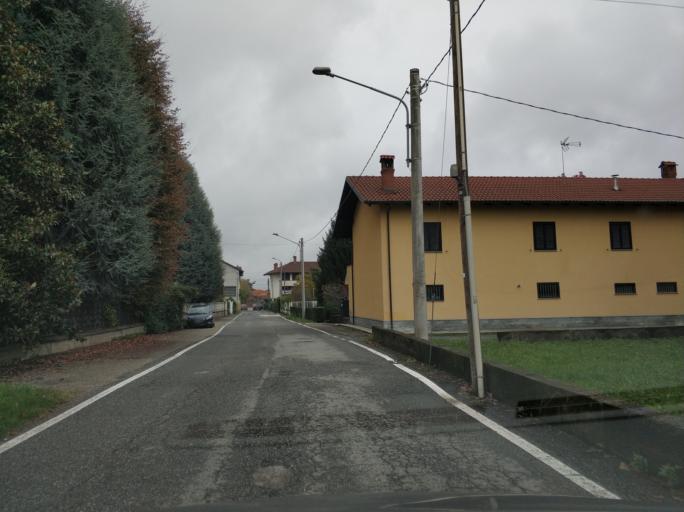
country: IT
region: Piedmont
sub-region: Provincia di Torino
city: Villanova Canavese
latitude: 45.2403
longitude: 7.5570
